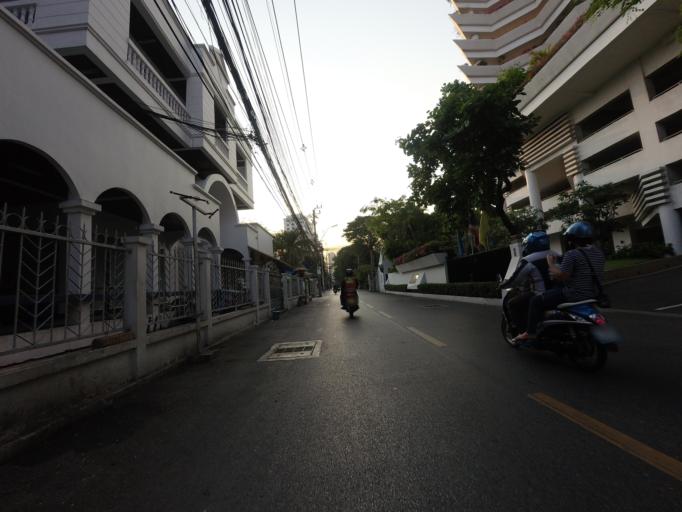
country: TH
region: Bangkok
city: Watthana
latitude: 13.7289
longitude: 100.5894
